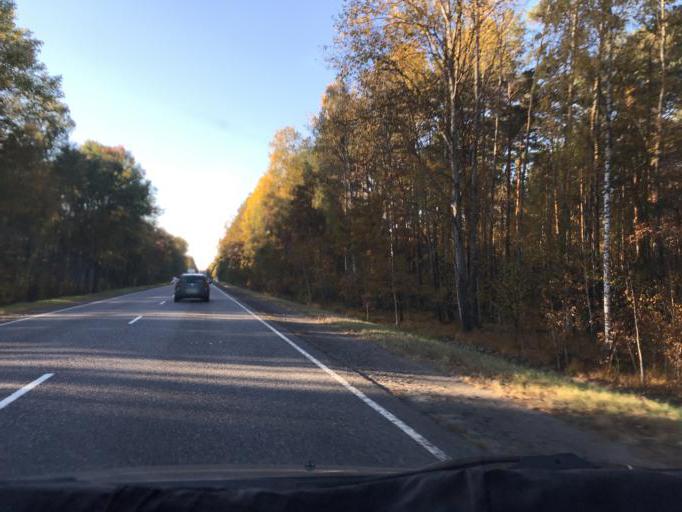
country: BY
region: Gomel
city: Pyetrykaw
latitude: 52.2511
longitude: 28.3641
